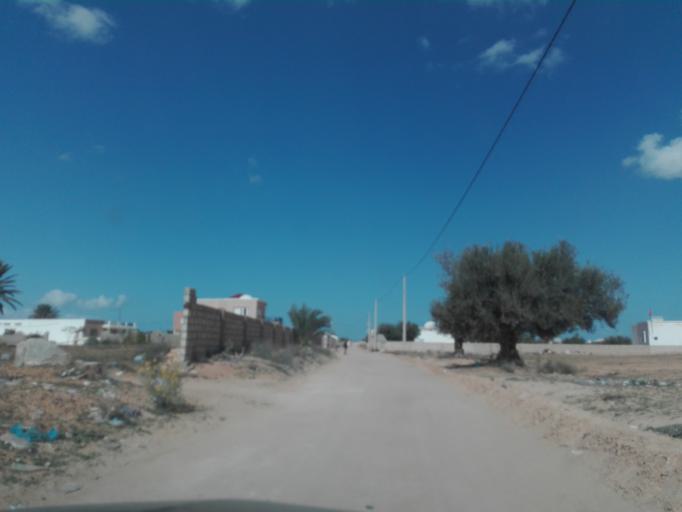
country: TN
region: Madanin
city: Bin Qirdan
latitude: 33.1605
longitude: 11.1950
